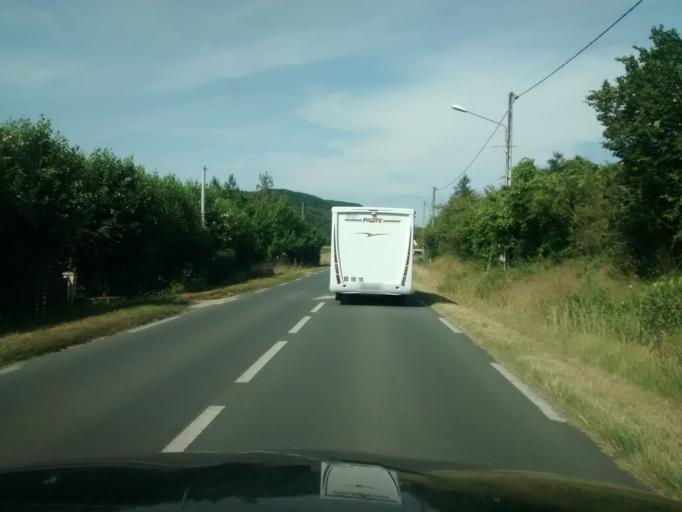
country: FR
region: Aquitaine
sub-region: Departement de la Dordogne
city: Cenac-et-Saint-Julien
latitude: 44.8338
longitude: 1.1595
